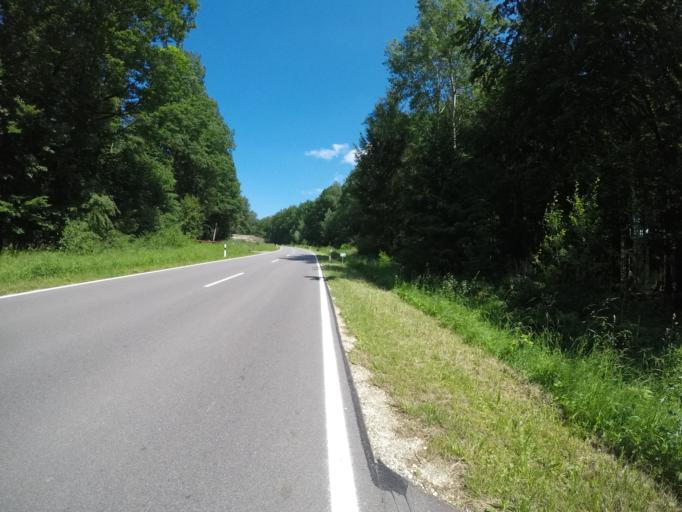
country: DE
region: Bavaria
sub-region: Lower Bavaria
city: Essing
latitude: 48.9084
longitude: 11.7859
